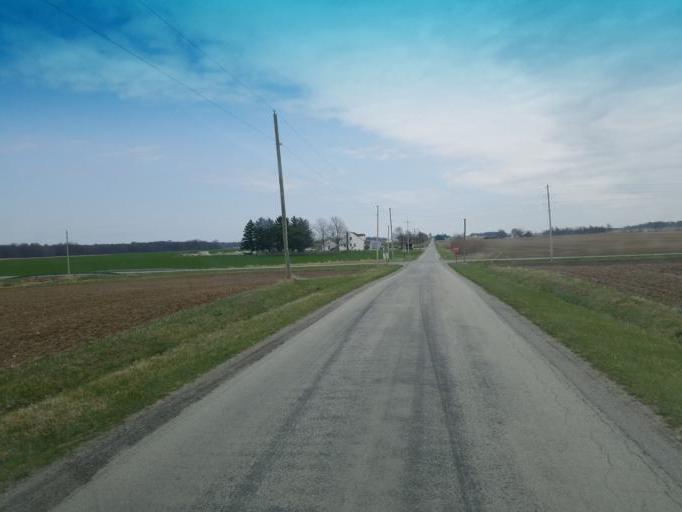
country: US
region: Ohio
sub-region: Wyandot County
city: Upper Sandusky
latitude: 40.8625
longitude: -83.1711
